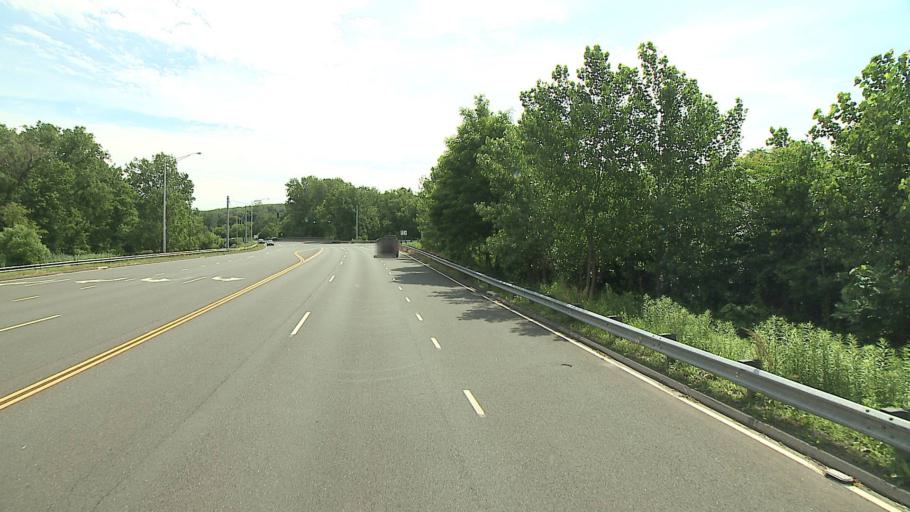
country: US
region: Connecticut
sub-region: Fairfield County
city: Danbury
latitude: 41.4208
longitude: -73.4186
